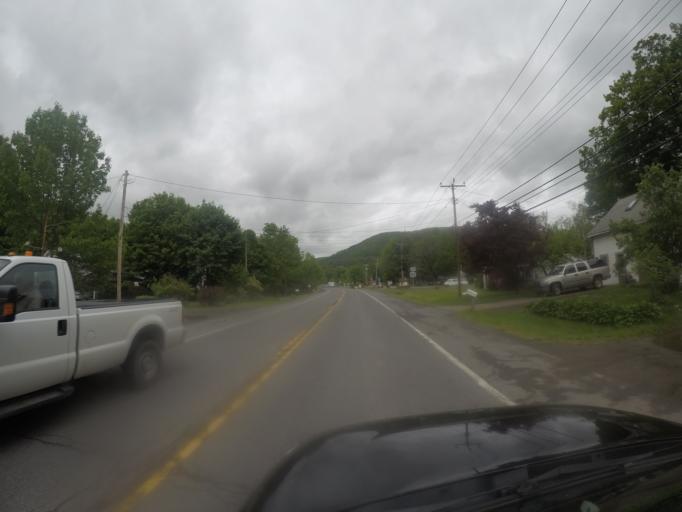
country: US
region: New York
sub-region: Ulster County
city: Shokan
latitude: 42.1192
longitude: -74.3909
